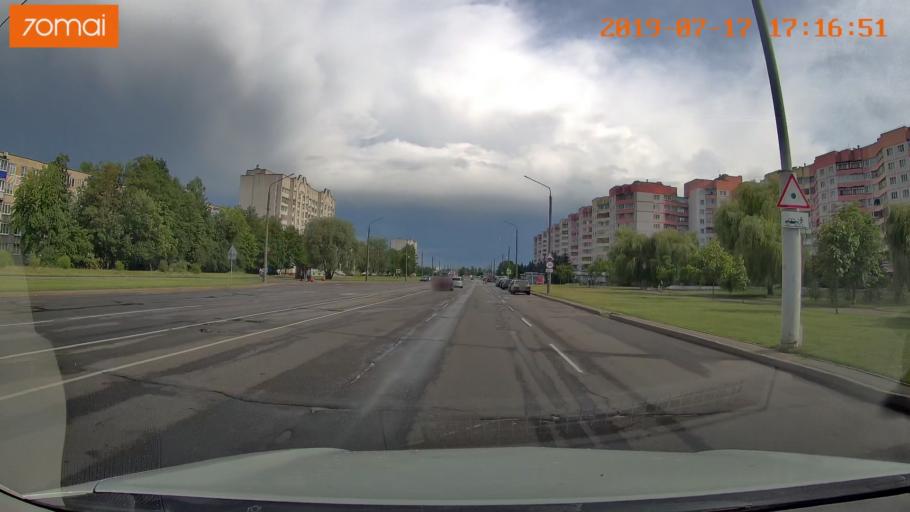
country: BY
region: Mogilev
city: Babruysk
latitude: 53.1648
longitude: 29.1958
